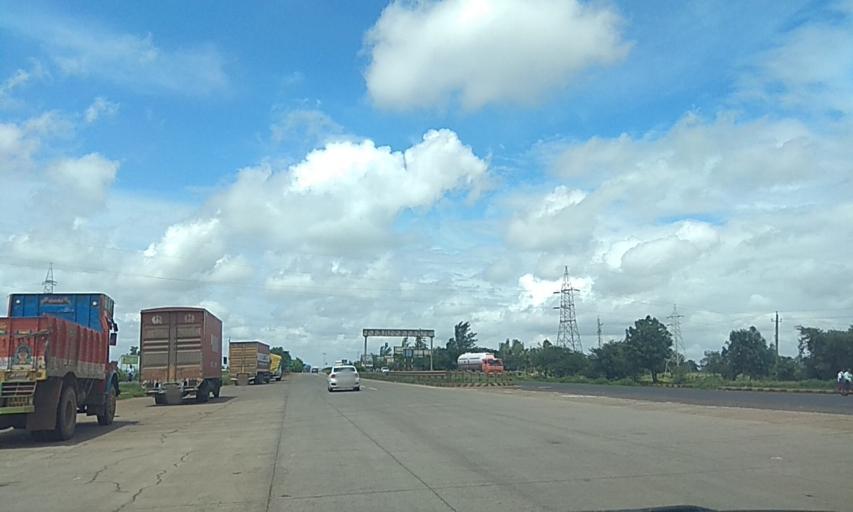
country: IN
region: Karnataka
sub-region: Belgaum
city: Sankeshwar
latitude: 16.1444
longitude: 74.5169
